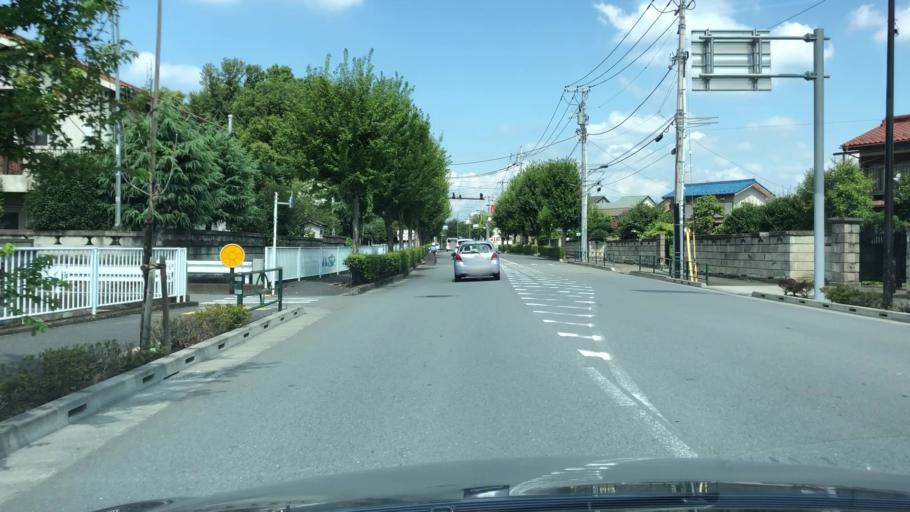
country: JP
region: Tokyo
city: Hino
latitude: 35.6856
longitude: 139.3801
